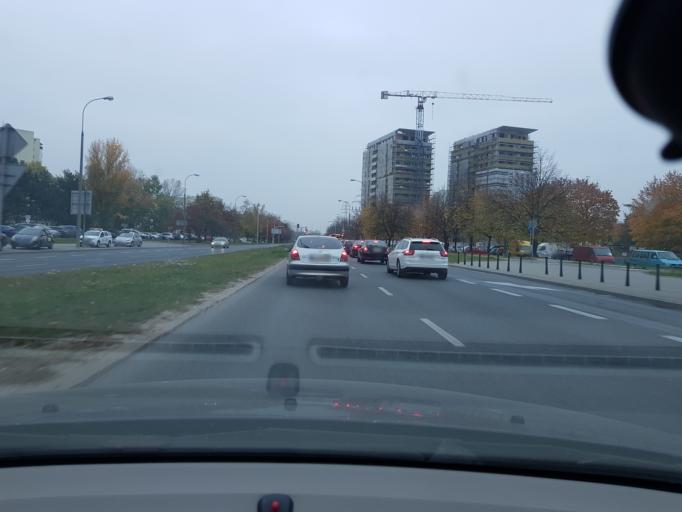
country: PL
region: Masovian Voivodeship
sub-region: Warszawa
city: Ursynow
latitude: 52.1500
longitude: 21.0334
